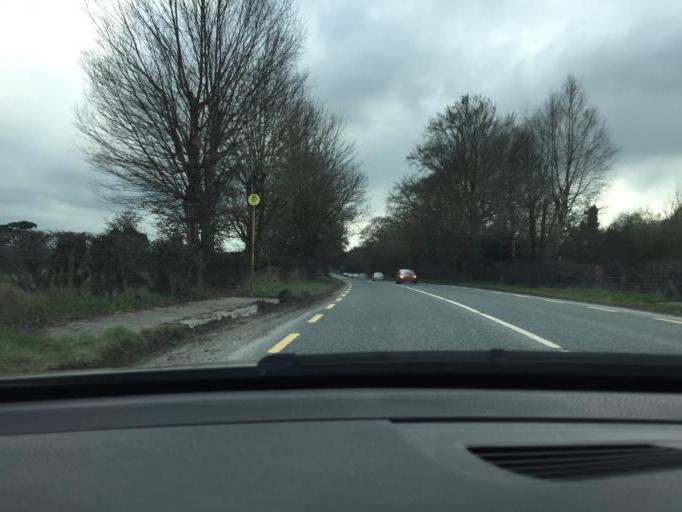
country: IE
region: Leinster
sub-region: South Dublin
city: Rathcoole
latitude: 53.2238
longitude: -6.4672
